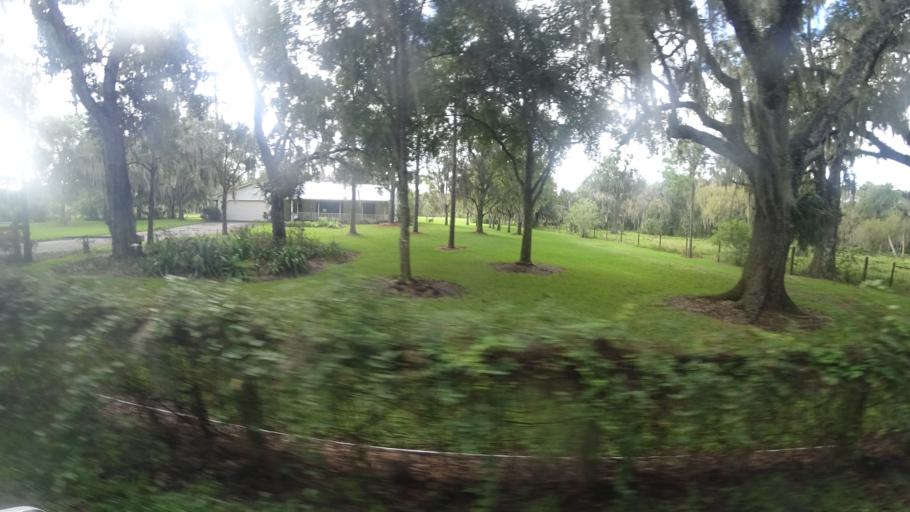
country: US
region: Florida
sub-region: Manatee County
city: Ellenton
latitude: 27.5709
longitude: -82.4342
